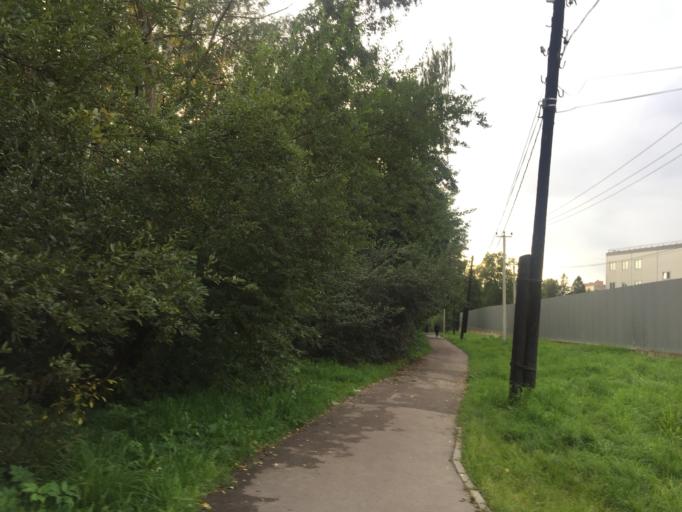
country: RU
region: Leningrad
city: Murino
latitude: 60.0423
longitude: 30.4715
